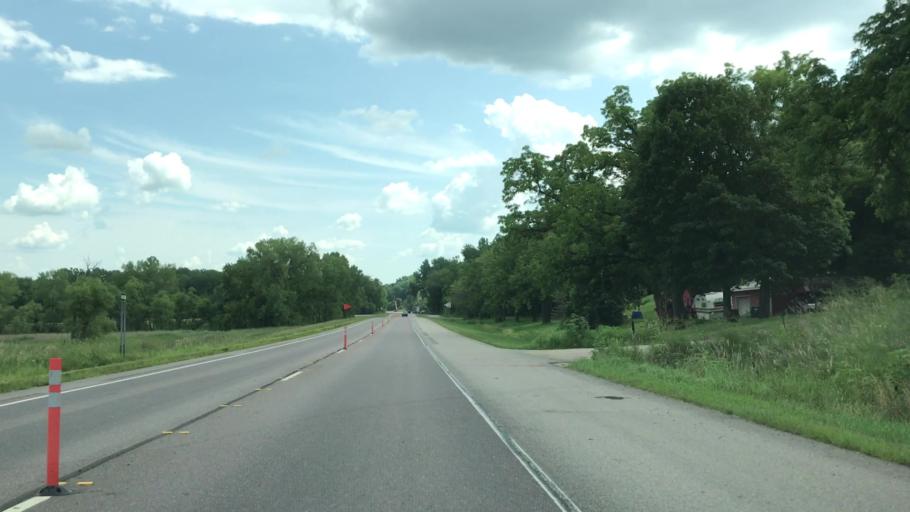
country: US
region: Minnesota
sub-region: Nicollet County
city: Saint Peter
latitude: 44.3735
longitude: -93.9674
